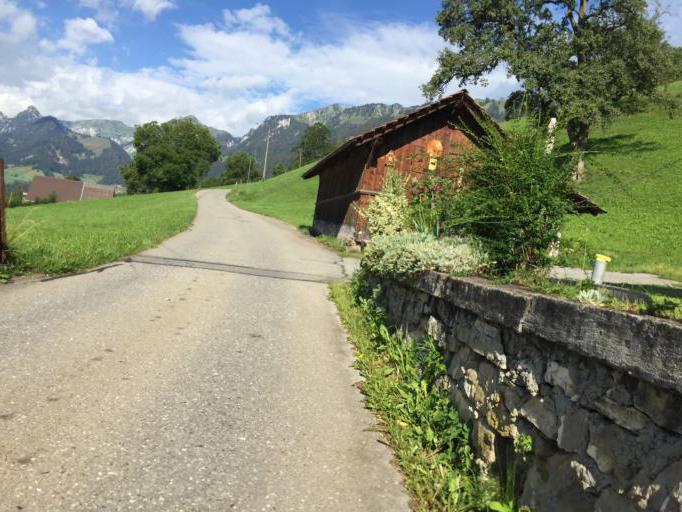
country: CH
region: Bern
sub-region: Obersimmental-Saanen District
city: Boltigen
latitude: 46.6600
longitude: 7.4614
